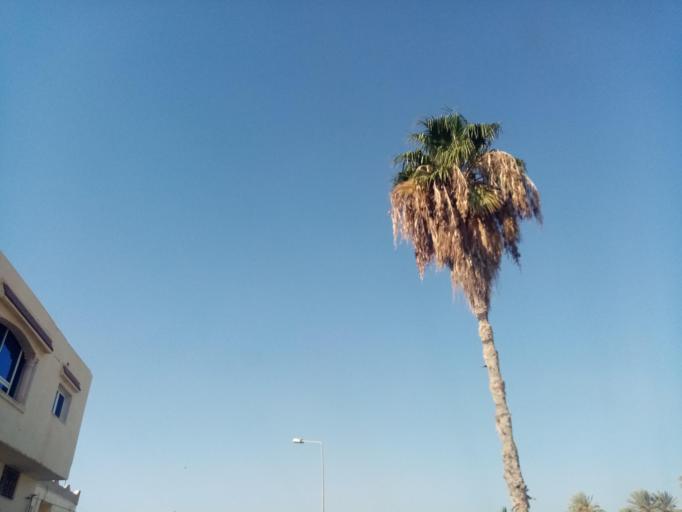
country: TN
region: Qabis
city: Gabes
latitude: 33.8904
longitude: 10.0958
